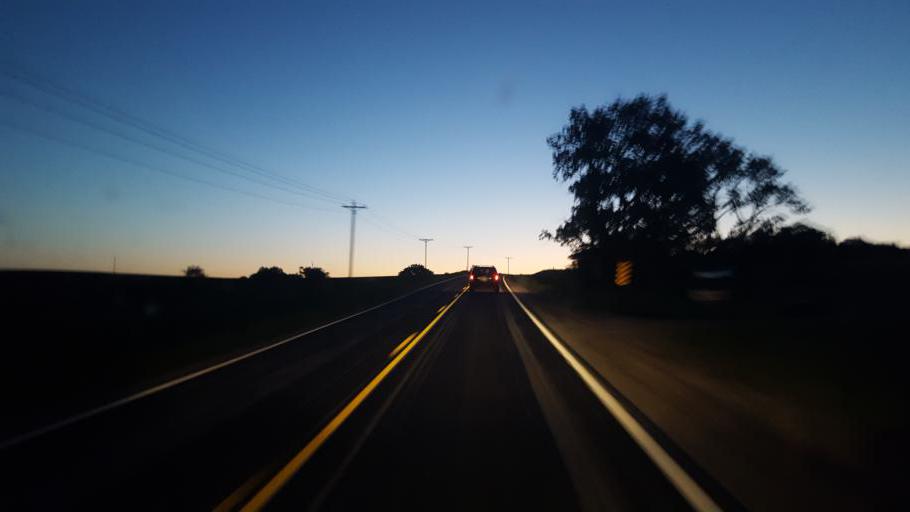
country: US
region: Missouri
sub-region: Mercer County
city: Princeton
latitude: 40.4083
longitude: -93.5489
